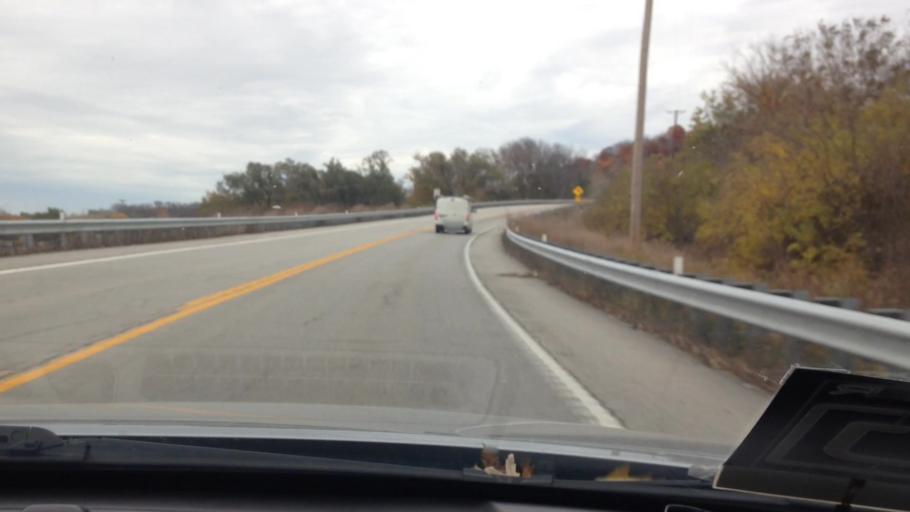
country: US
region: Missouri
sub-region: Platte County
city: Weston
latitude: 39.3642
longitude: -94.8753
